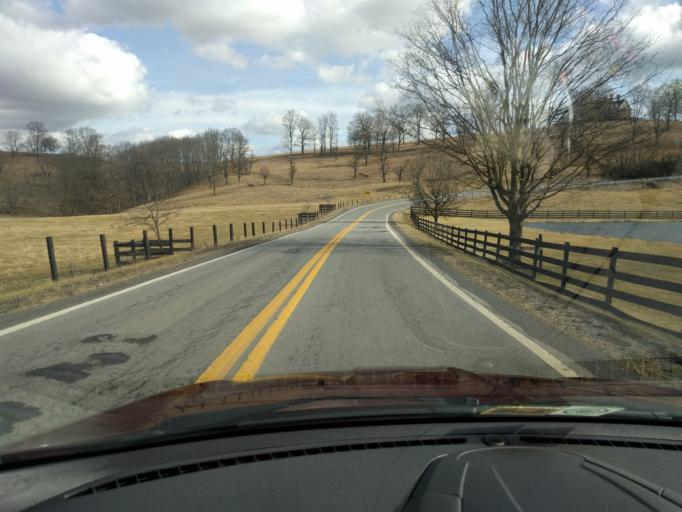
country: US
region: West Virginia
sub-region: Greenbrier County
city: Lewisburg
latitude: 37.8232
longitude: -80.4777
